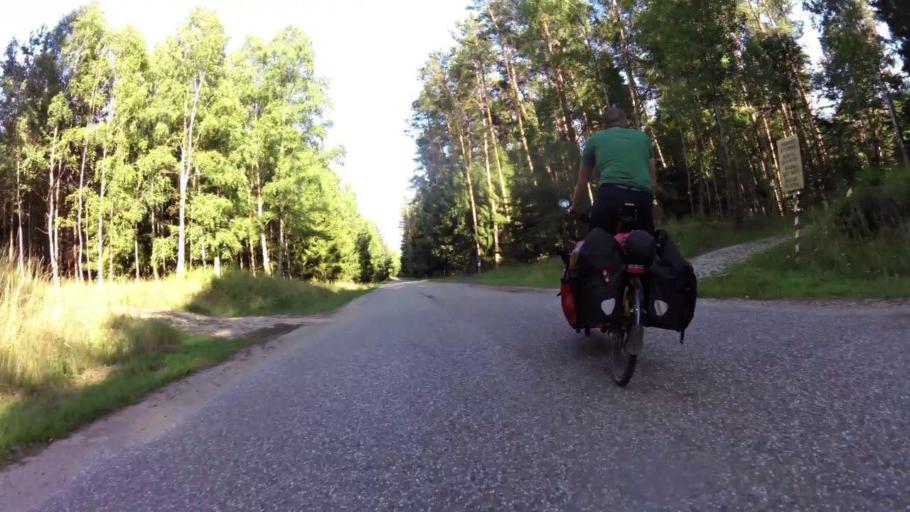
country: PL
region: West Pomeranian Voivodeship
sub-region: Powiat drawski
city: Drawsko Pomorskie
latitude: 53.4646
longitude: 15.8509
